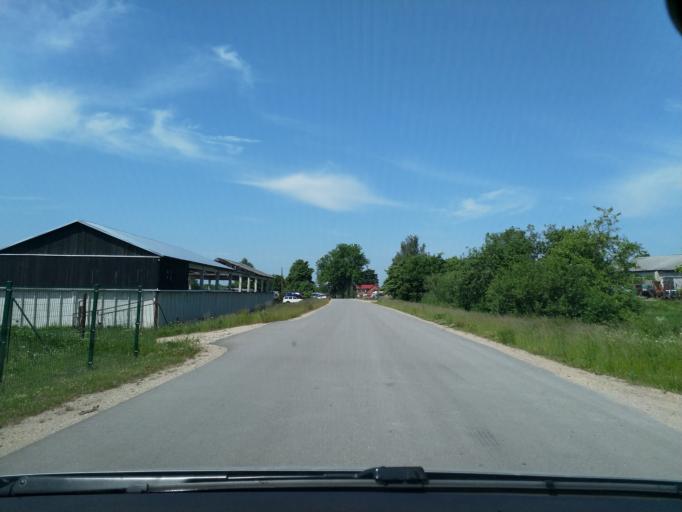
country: LV
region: Kuldigas Rajons
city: Kuldiga
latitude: 56.9584
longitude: 22.0113
